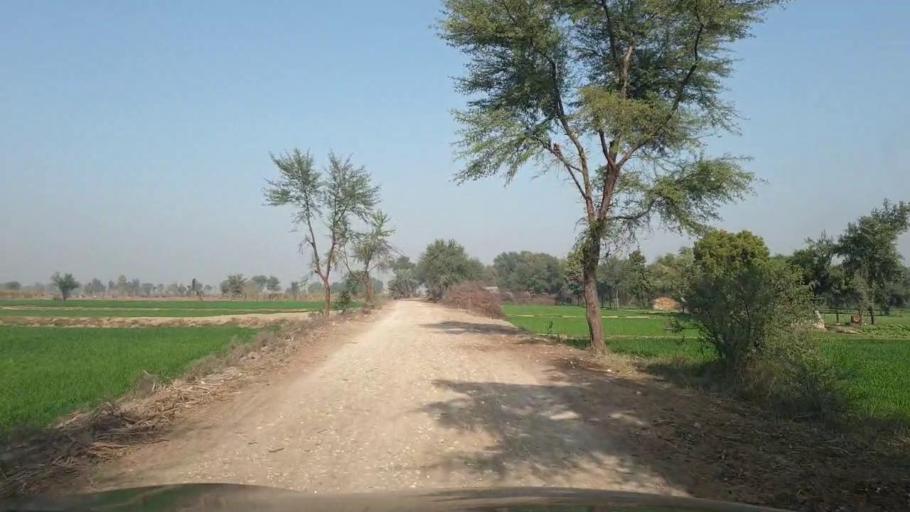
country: PK
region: Sindh
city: Ubauro
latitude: 28.1196
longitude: 69.7510
